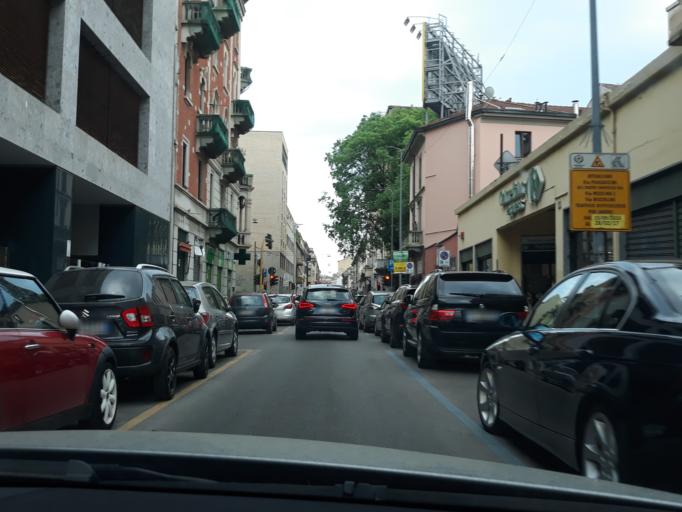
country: IT
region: Lombardy
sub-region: Citta metropolitana di Milano
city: Milano
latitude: 45.4842
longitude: 9.1701
